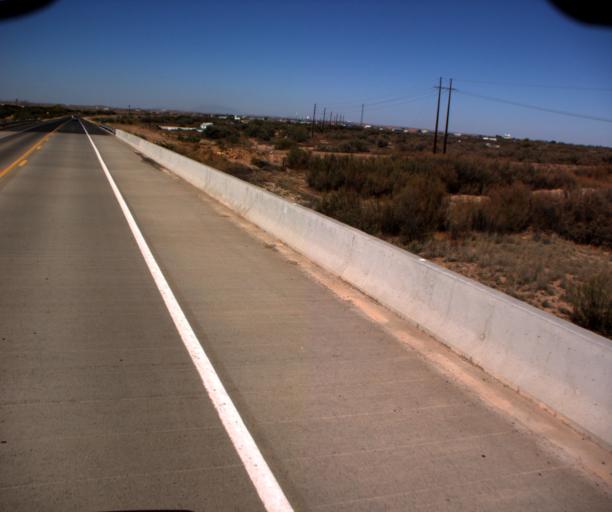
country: US
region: Arizona
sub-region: Navajo County
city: Winslow
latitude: 35.0067
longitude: -110.6534
